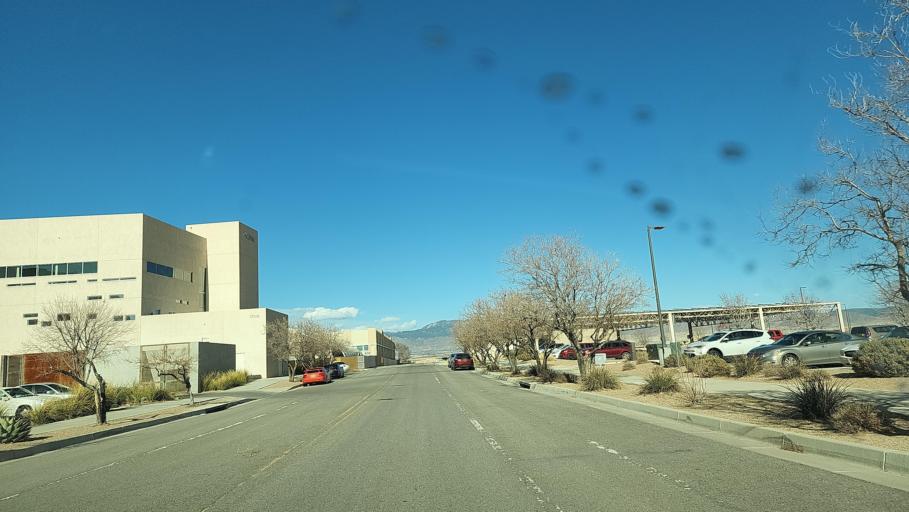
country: US
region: New Mexico
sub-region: Bernalillo County
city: South Valley
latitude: 34.9862
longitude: -106.6130
